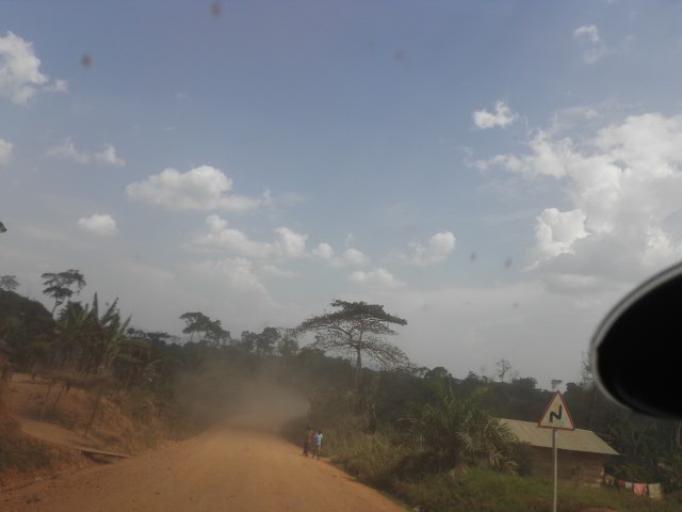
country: CD
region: Nord Kivu
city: Beni
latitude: 0.9820
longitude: 29.5875
